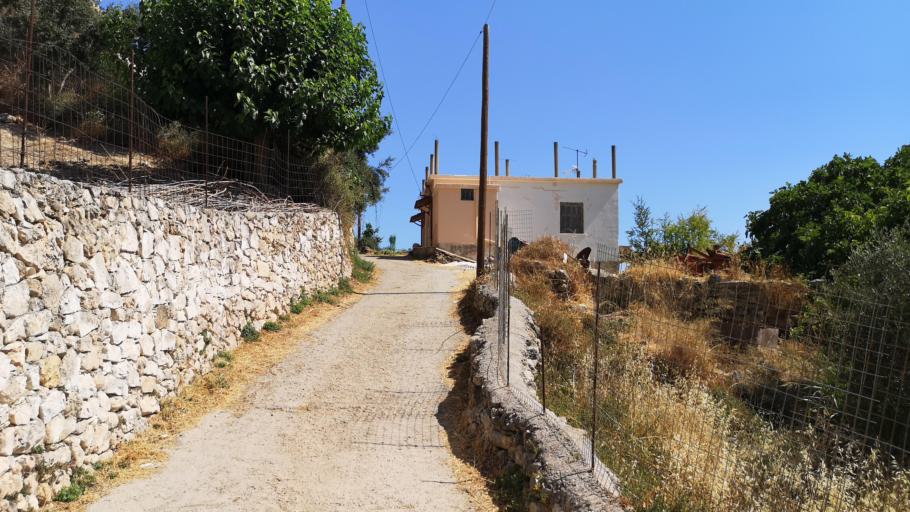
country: GR
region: Crete
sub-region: Nomos Chanias
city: Kalivai
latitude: 35.3983
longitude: 24.1345
